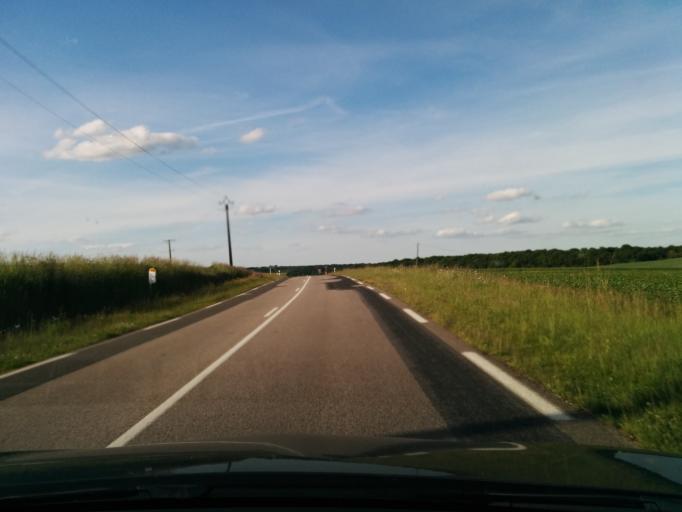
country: FR
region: Haute-Normandie
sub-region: Departement de l'Eure
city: Charleval
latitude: 49.3369
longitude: 1.4494
